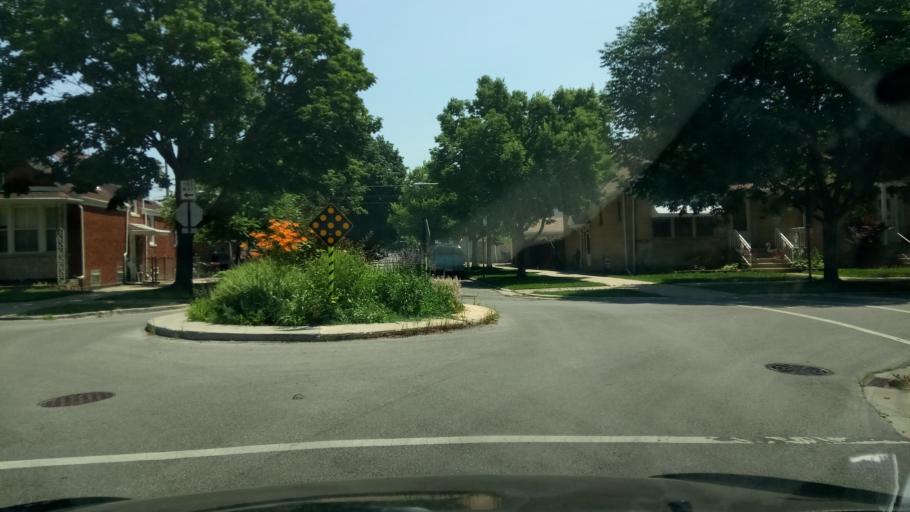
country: US
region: Illinois
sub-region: Cook County
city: Hometown
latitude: 41.7822
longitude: -87.7355
